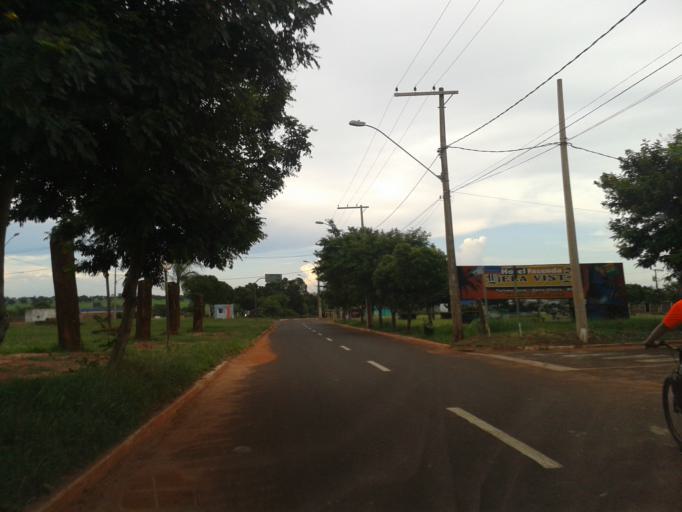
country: BR
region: Minas Gerais
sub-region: Santa Vitoria
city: Santa Vitoria
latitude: -18.8539
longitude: -50.1304
